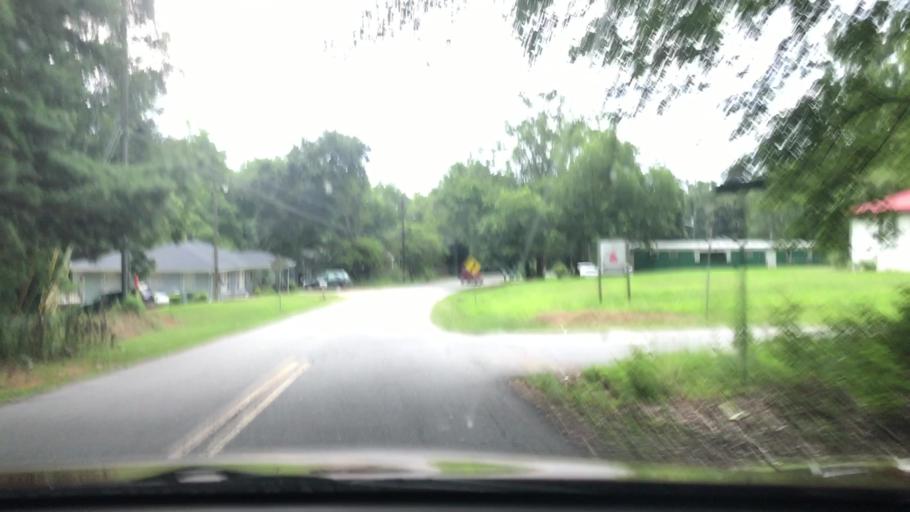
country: US
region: Georgia
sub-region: Barrow County
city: Winder
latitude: 33.9871
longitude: -83.7363
